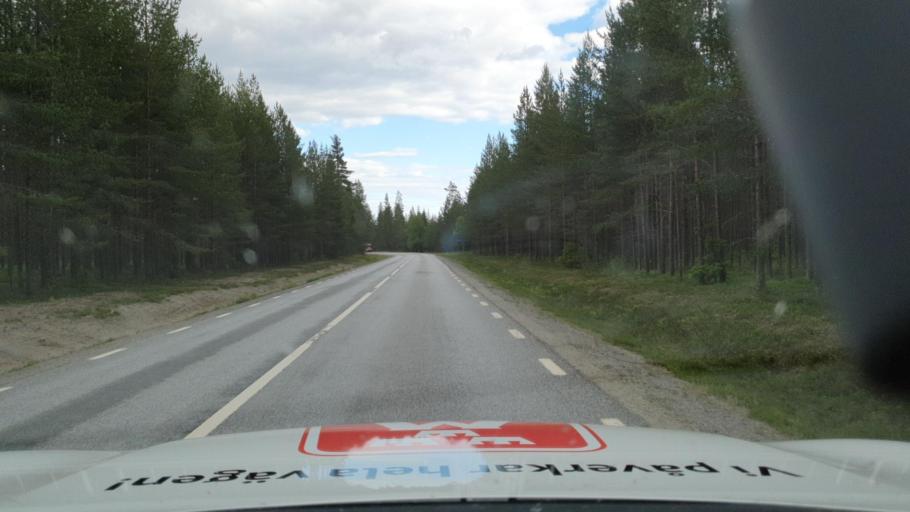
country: SE
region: Vaesterbotten
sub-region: Vindelns Kommun
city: Vindeln
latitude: 64.2501
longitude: 19.6420
